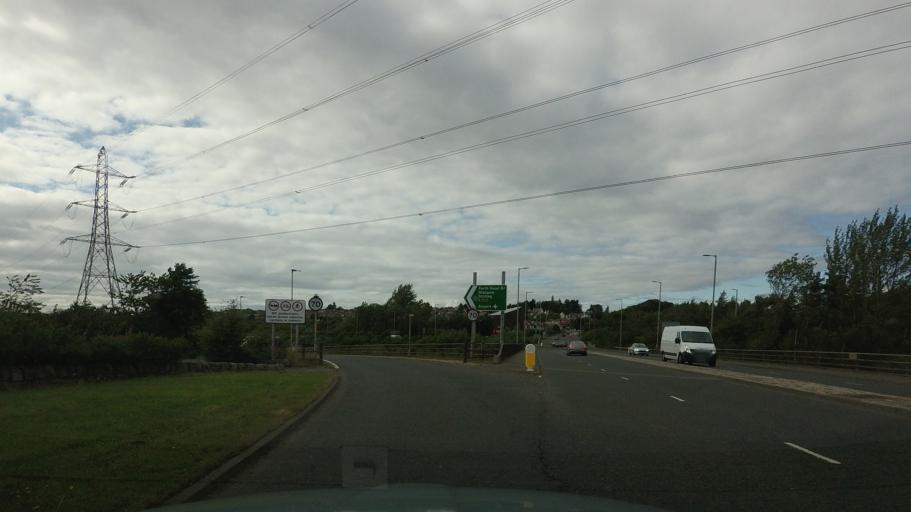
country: GB
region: Scotland
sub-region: Midlothian
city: Loanhead
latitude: 55.8954
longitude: -3.2025
